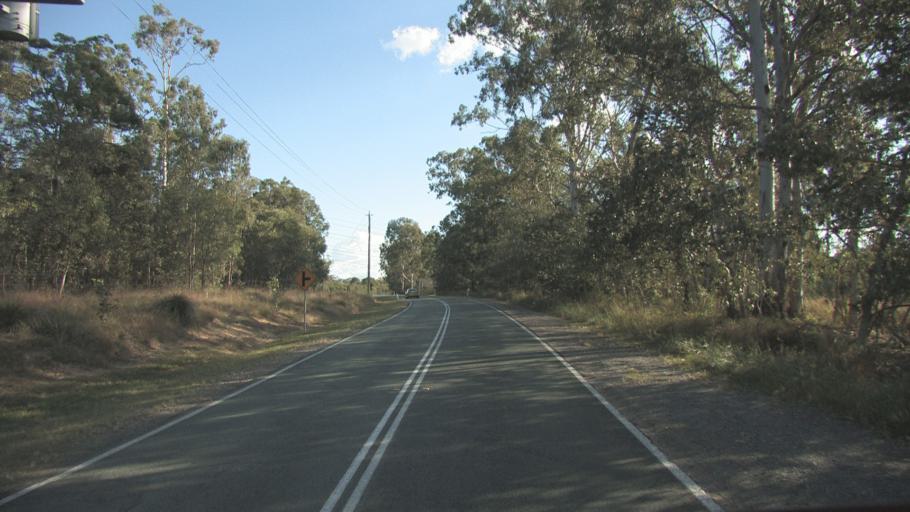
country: AU
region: Queensland
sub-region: Ipswich
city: Springfield Lakes
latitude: -27.7277
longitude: 152.9539
